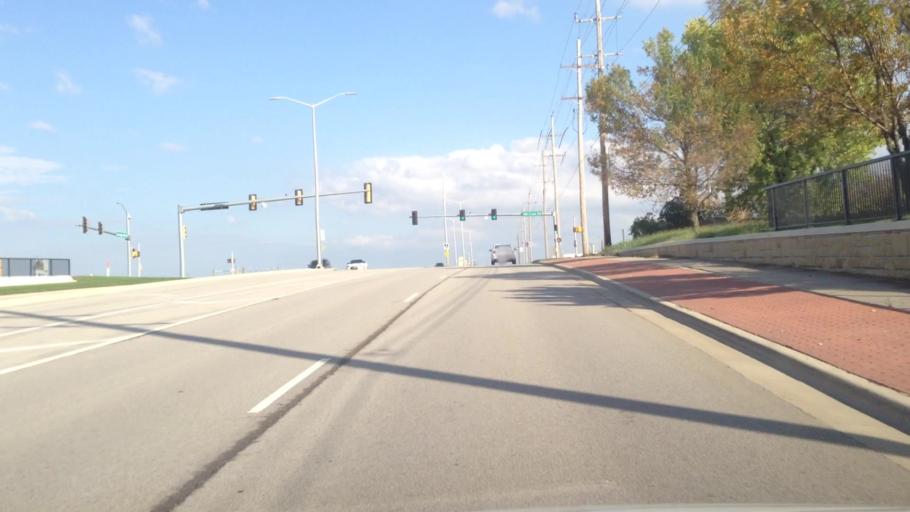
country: US
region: Kansas
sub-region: Johnson County
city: Olathe
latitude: 38.9272
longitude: -94.7895
